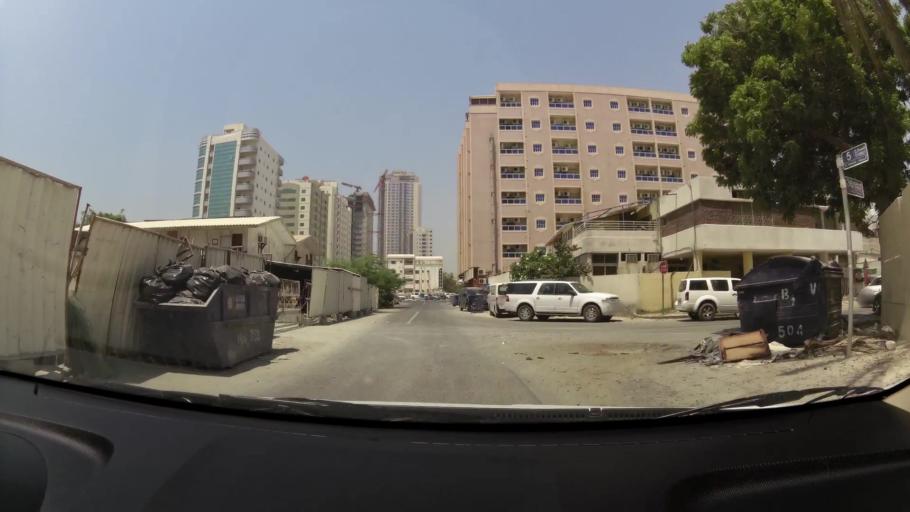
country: AE
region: Ajman
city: Ajman
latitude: 25.4058
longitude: 55.4319
